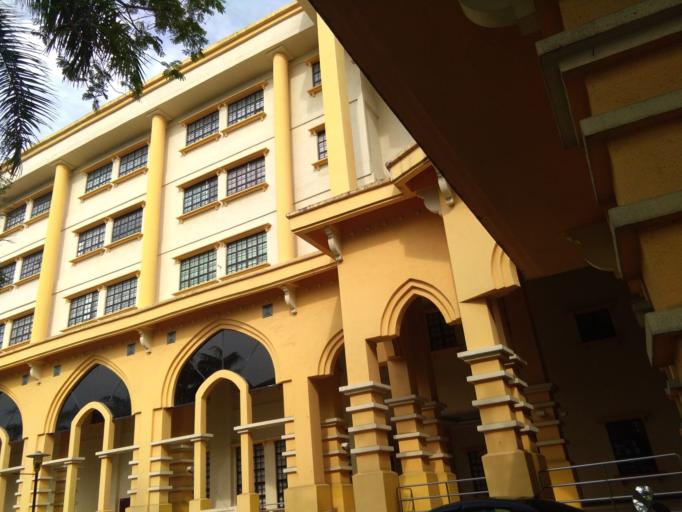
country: MY
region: Perak
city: Ipoh
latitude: 4.6015
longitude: 101.0929
